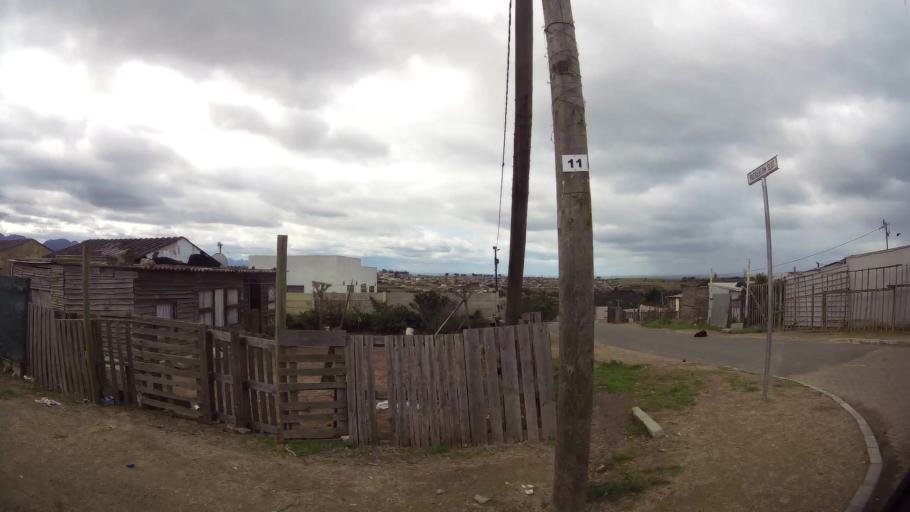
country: ZA
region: Western Cape
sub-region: Eden District Municipality
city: George
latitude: -34.0180
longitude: 22.4811
